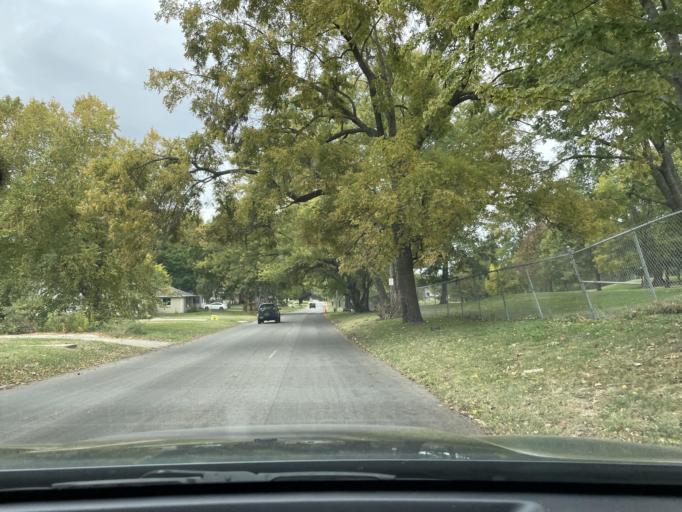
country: US
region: Missouri
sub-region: Buchanan County
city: Saint Joseph
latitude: 39.7692
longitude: -94.8156
